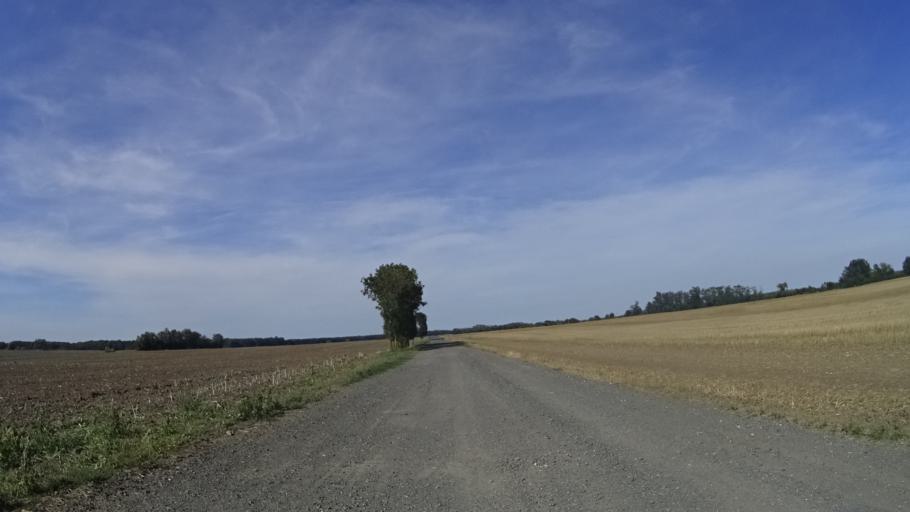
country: AT
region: Lower Austria
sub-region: Politischer Bezirk Ganserndorf
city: Durnkrut
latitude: 48.4350
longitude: 16.8716
